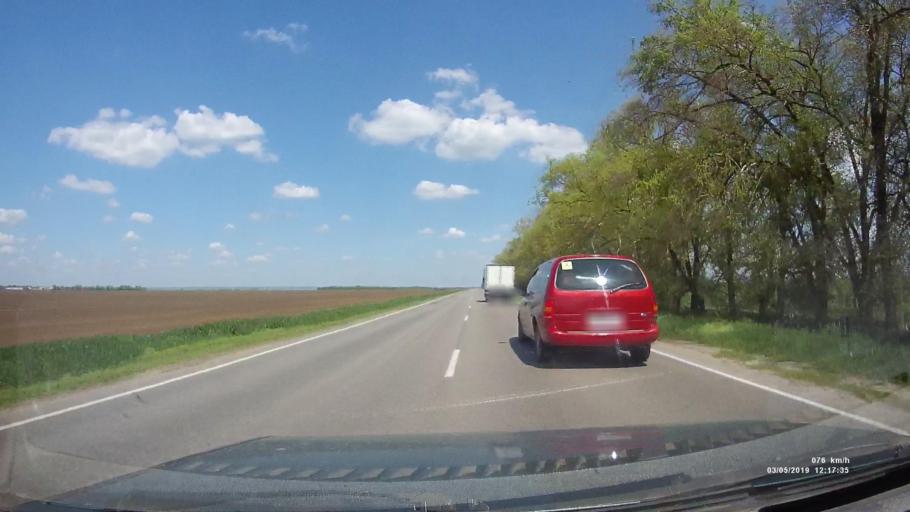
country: RU
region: Rostov
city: Melikhovskaya
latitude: 47.3840
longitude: 40.5931
